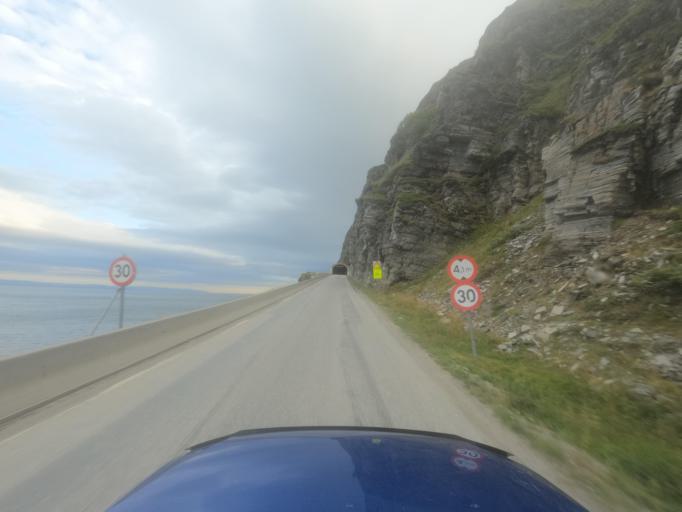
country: NO
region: Finnmark Fylke
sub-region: Porsanger
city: Lakselv
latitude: 70.6185
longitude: 25.3408
